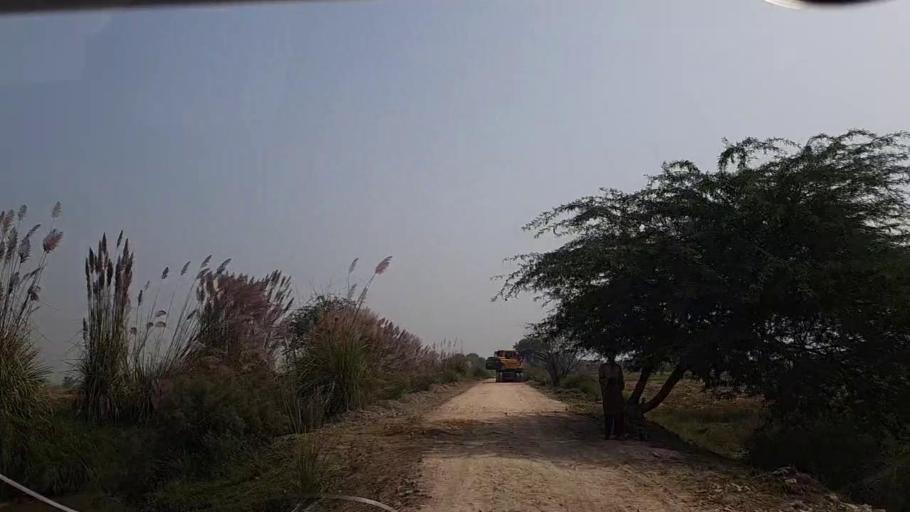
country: PK
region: Sindh
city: Garhi Yasin
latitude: 27.9207
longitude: 68.5782
